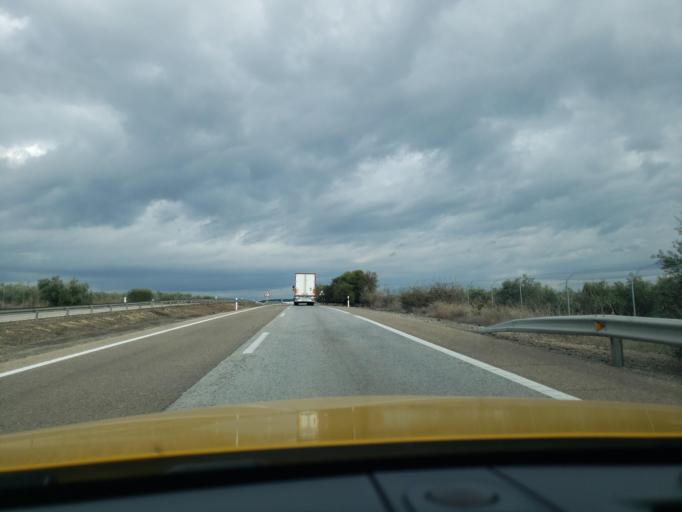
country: ES
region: Andalusia
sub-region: Provincia de Jaen
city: Banos de la Encina
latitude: 38.1400
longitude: -3.7370
